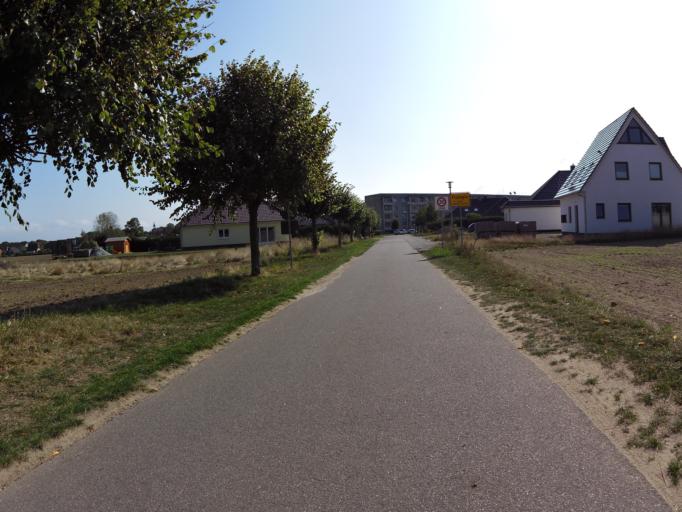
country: DE
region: Mecklenburg-Vorpommern
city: Loddin
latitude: 53.9687
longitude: 14.0582
